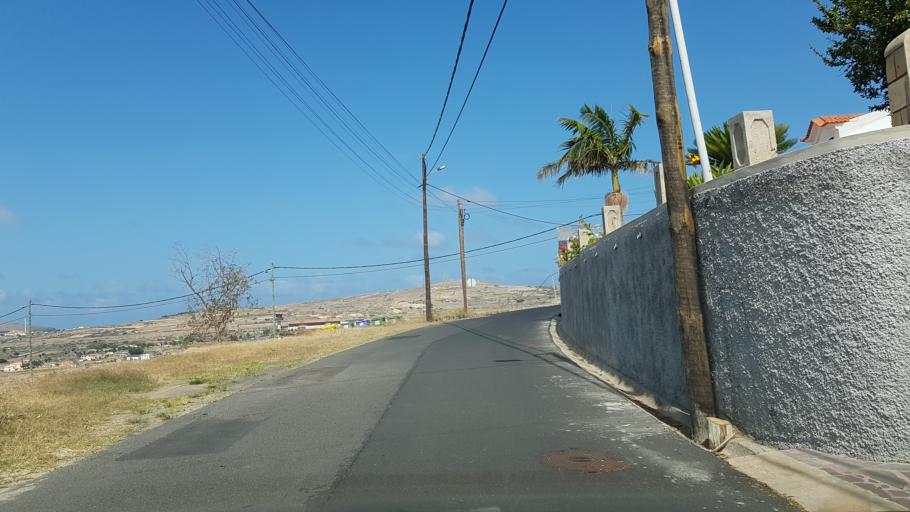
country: PT
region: Madeira
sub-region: Porto Santo
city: Vila de Porto Santo
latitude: 33.0712
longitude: -16.3311
